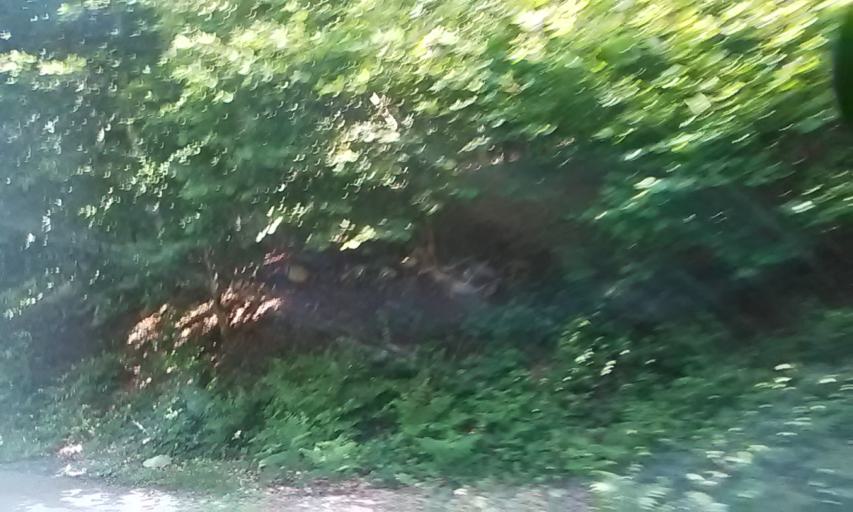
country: IT
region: Piedmont
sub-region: Provincia di Vercelli
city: Civiasco
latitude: 45.8378
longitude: 8.3025
